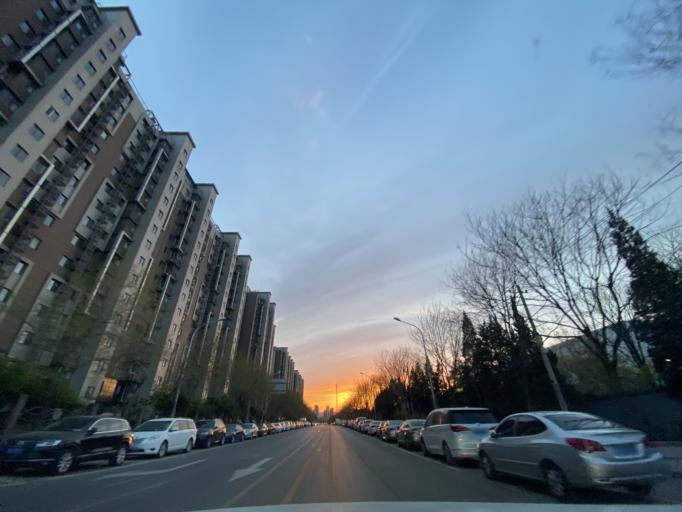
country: CN
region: Beijing
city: Qinghe
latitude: 40.0163
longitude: 116.3623
